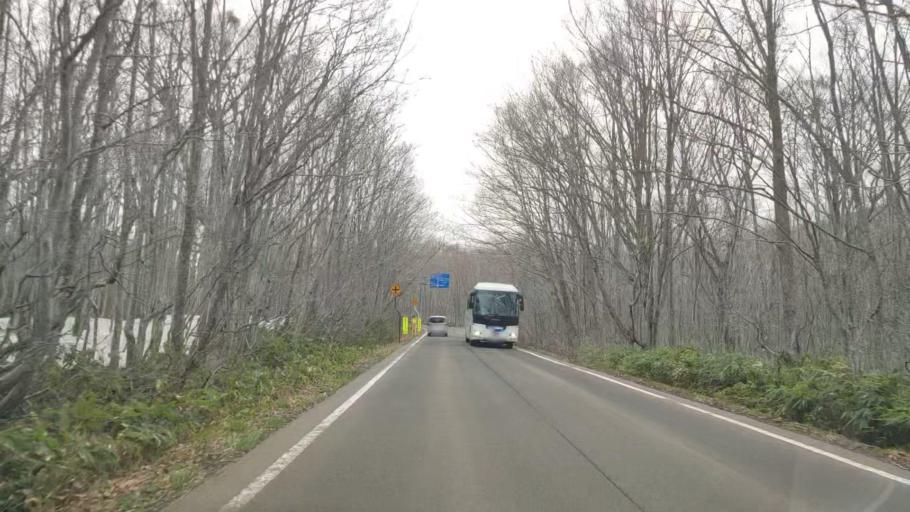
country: JP
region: Aomori
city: Aomori Shi
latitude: 40.6649
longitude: 140.9570
